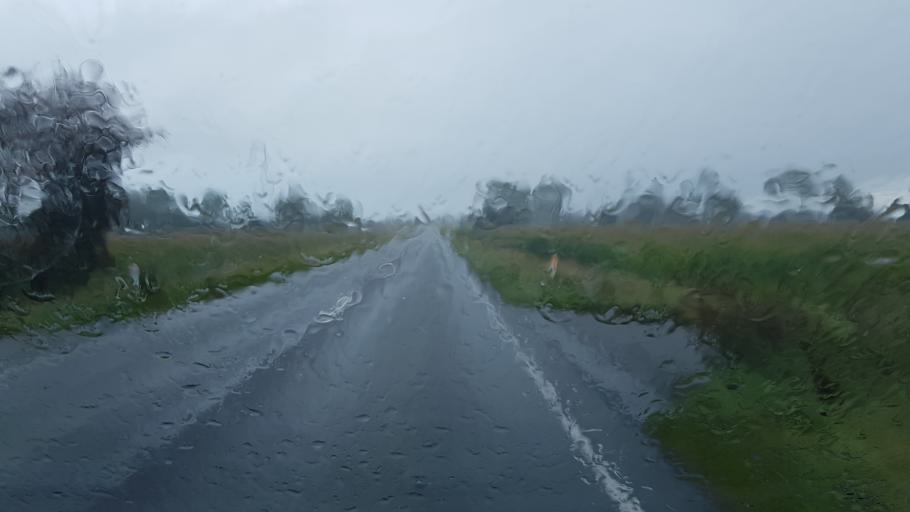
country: DK
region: South Denmark
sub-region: Kolding Kommune
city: Vamdrup
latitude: 55.3499
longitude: 9.2329
